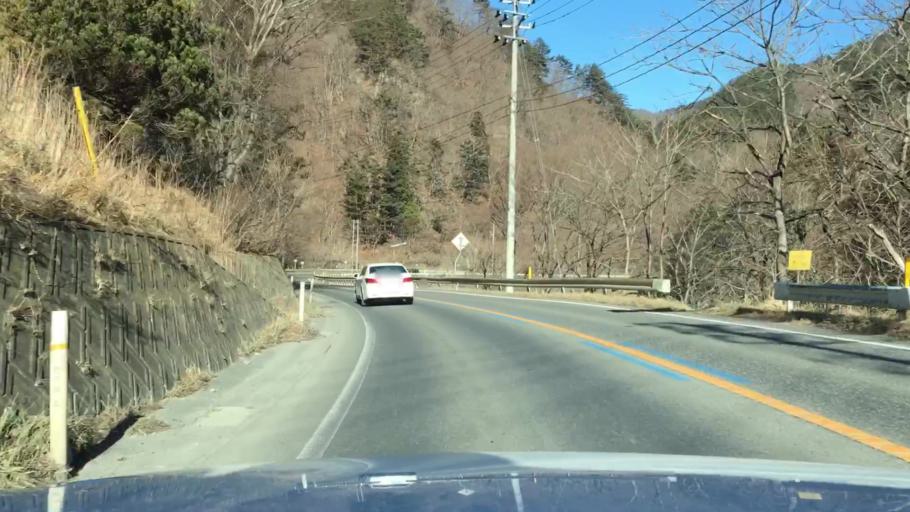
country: JP
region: Iwate
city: Miyako
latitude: 39.6045
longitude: 141.7730
